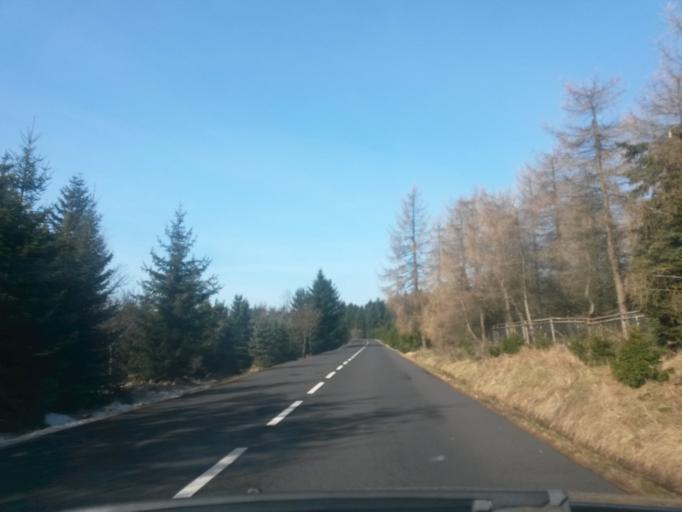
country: CZ
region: Ustecky
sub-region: Okres Chomutov
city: Kovarska
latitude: 50.4142
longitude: 13.0711
